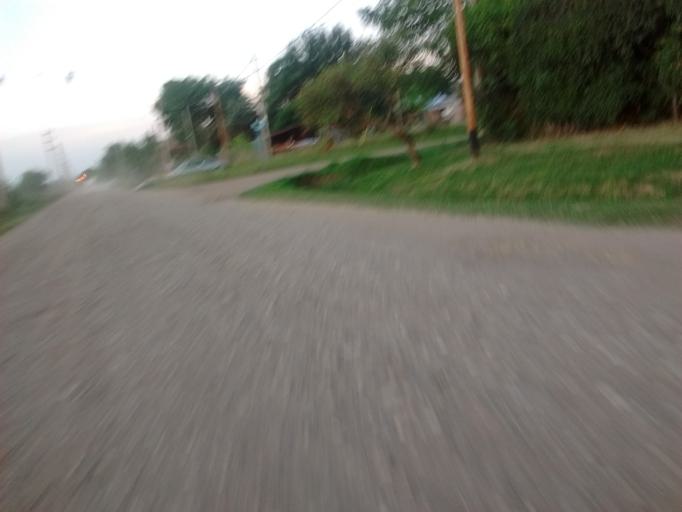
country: AR
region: Santa Fe
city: Funes
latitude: -32.9094
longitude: -60.8161
